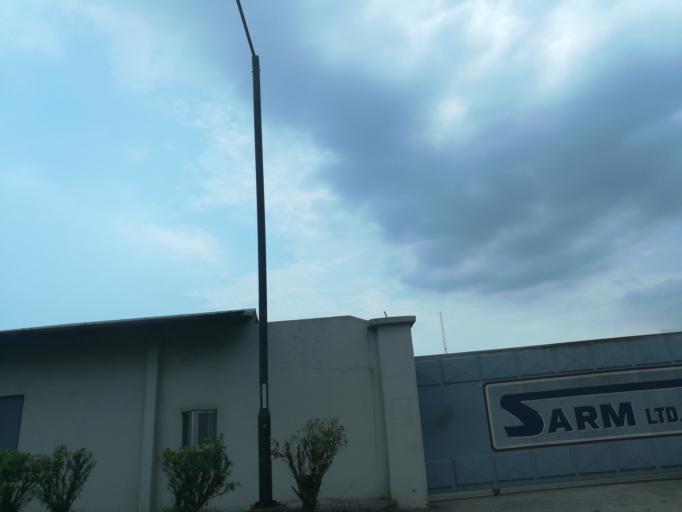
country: NG
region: Lagos
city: Ikeja
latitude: 6.6094
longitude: 3.3608
